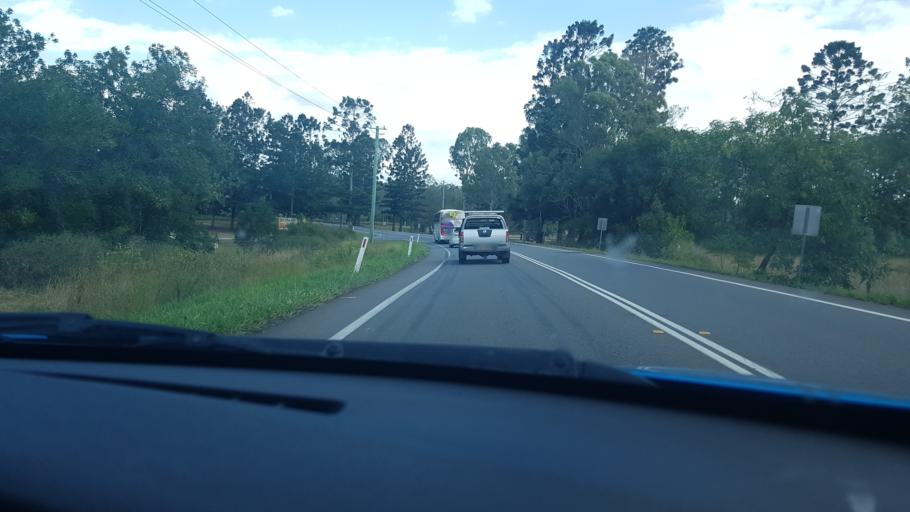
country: AU
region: Queensland
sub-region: Logan
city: North Maclean
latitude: -27.7822
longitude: 153.0117
